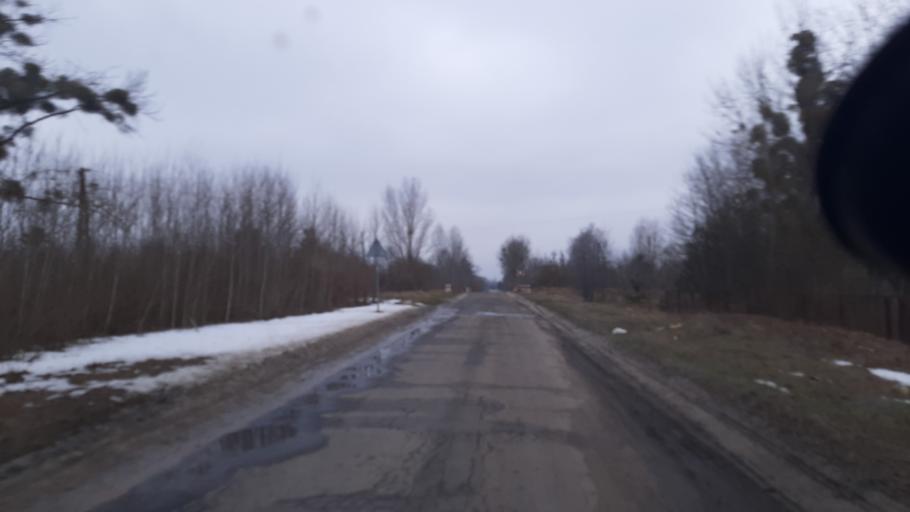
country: PL
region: Lublin Voivodeship
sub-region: Powiat wlodawski
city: Wlodawa
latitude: 51.5191
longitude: 23.5892
